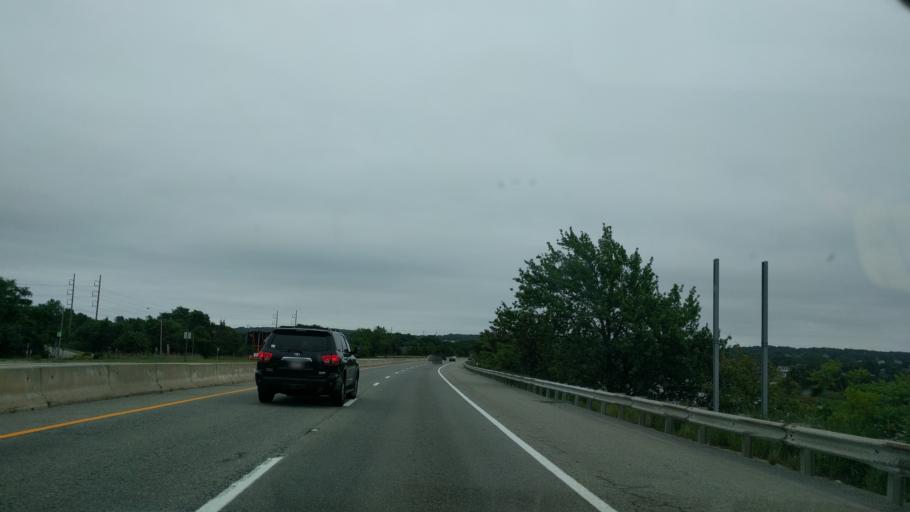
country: US
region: Rhode Island
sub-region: Newport County
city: Tiverton
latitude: 41.6370
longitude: -71.2295
